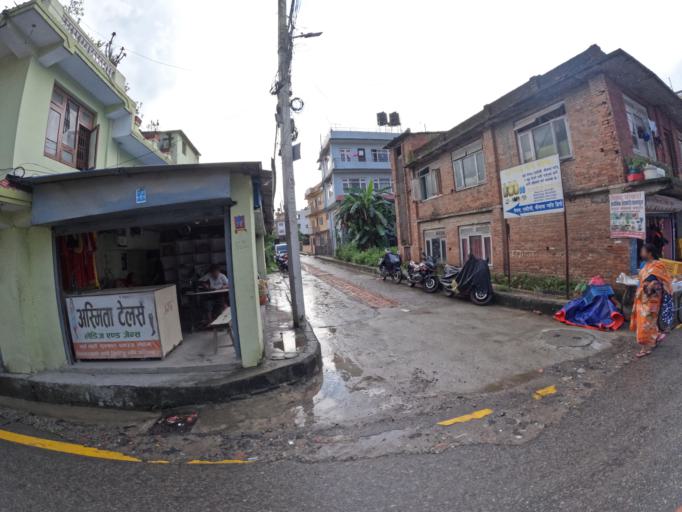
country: NP
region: Central Region
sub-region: Bagmati Zone
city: Kathmandu
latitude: 27.7506
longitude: 85.3254
